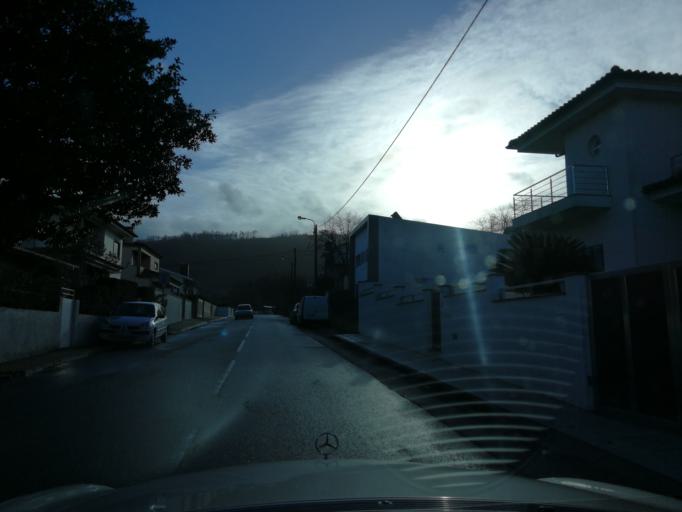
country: PT
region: Braga
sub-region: Braga
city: Braga
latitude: 41.5360
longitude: -8.4004
